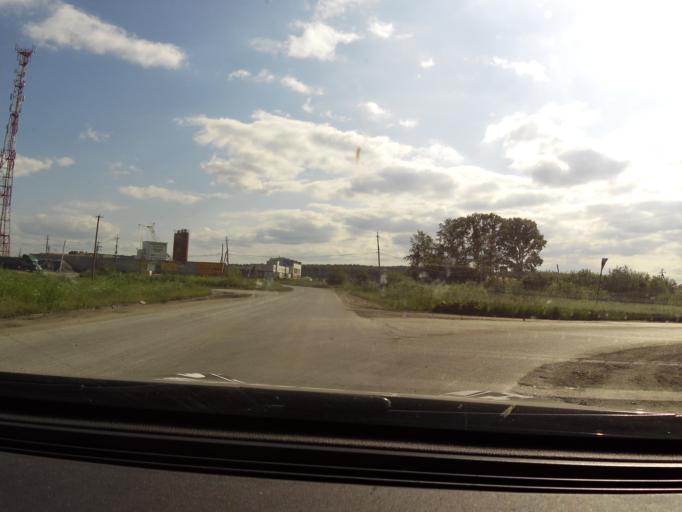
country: RU
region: Sverdlovsk
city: Shirokaya Rechka
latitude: 56.7896
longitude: 60.4820
